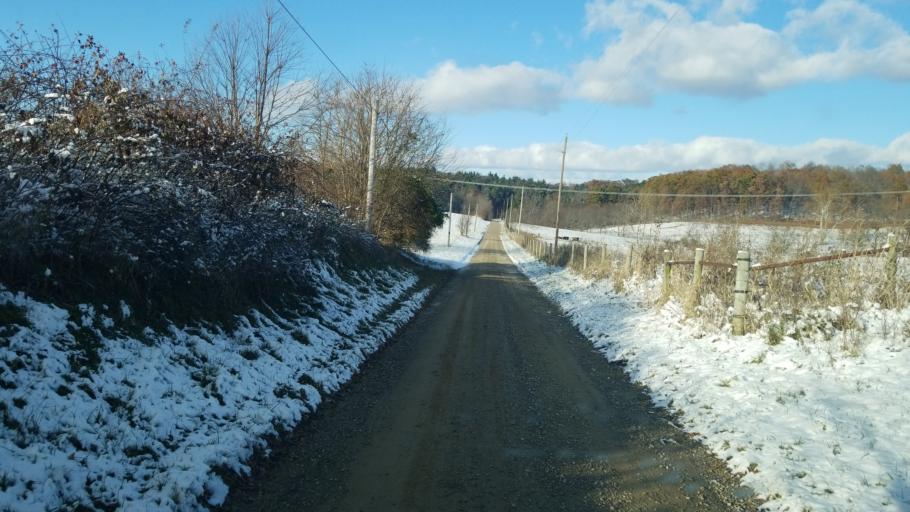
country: US
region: Ohio
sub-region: Licking County
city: Newark
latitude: 40.1482
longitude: -82.3888
